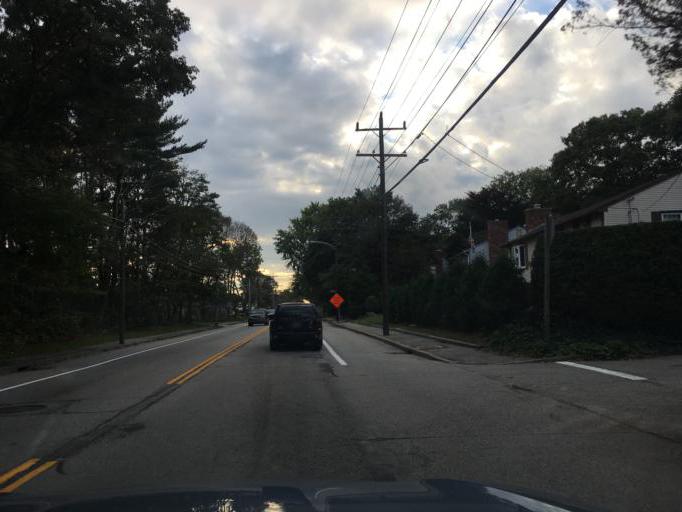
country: US
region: Rhode Island
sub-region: Kent County
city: Warwick
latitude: 41.7013
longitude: -71.4367
